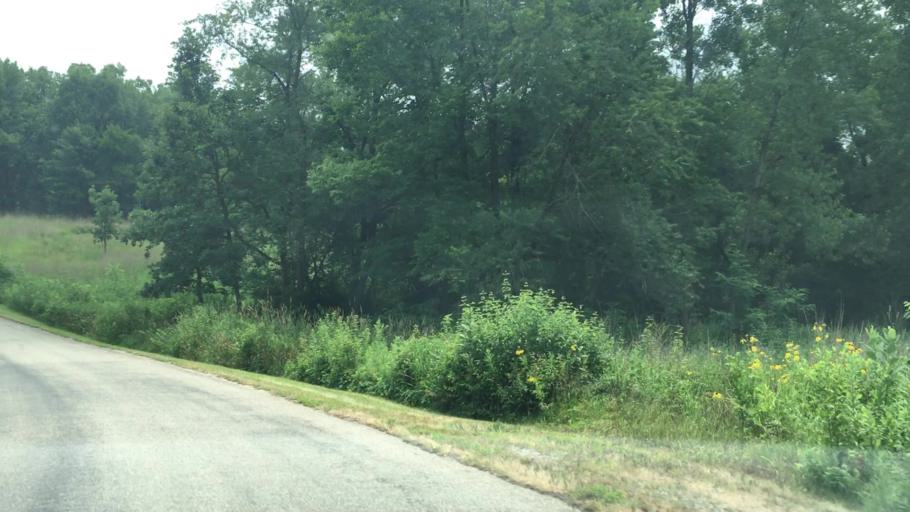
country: US
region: Iowa
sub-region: Johnson County
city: Tiffin
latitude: 41.7375
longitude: -91.7278
